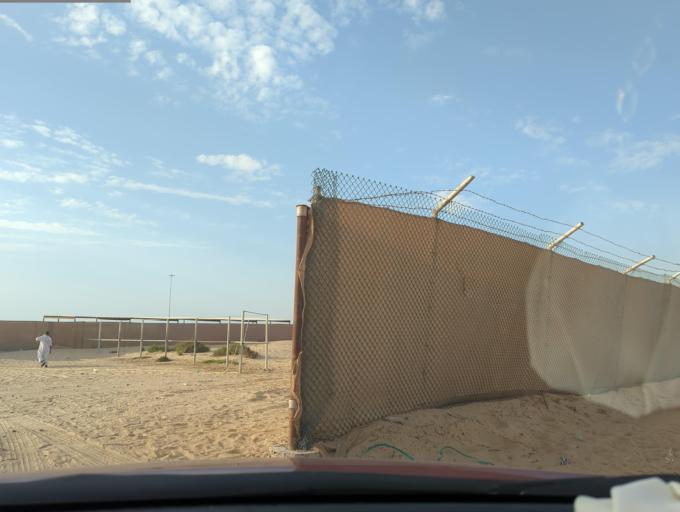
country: AE
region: Dubai
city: Dubai
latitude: 24.7194
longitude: 54.8670
